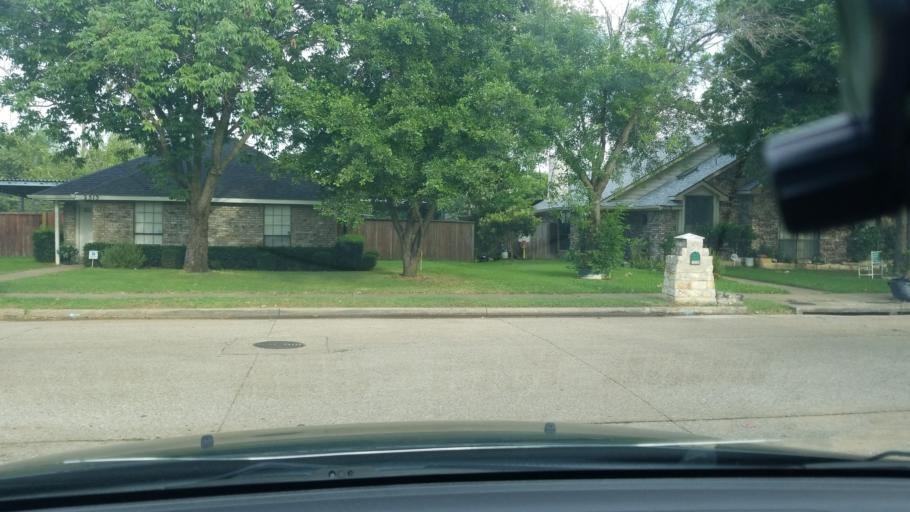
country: US
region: Texas
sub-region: Dallas County
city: Balch Springs
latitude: 32.7556
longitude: -96.6474
